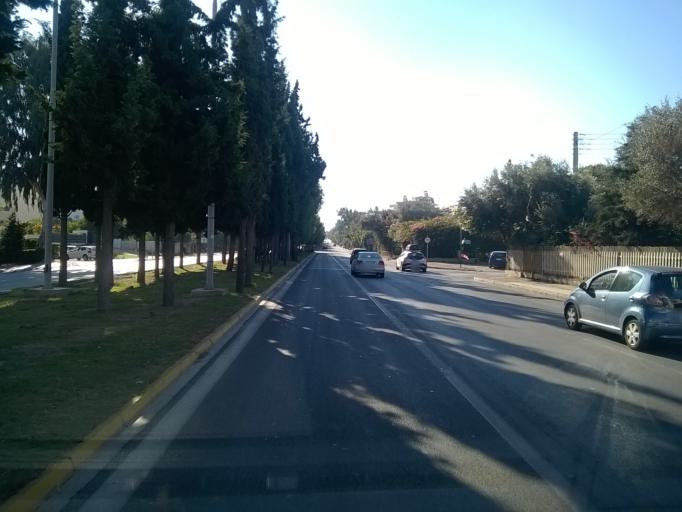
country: GR
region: Attica
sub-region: Nomarchia Anatolikis Attikis
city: Voula
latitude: 37.8318
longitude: 23.7728
